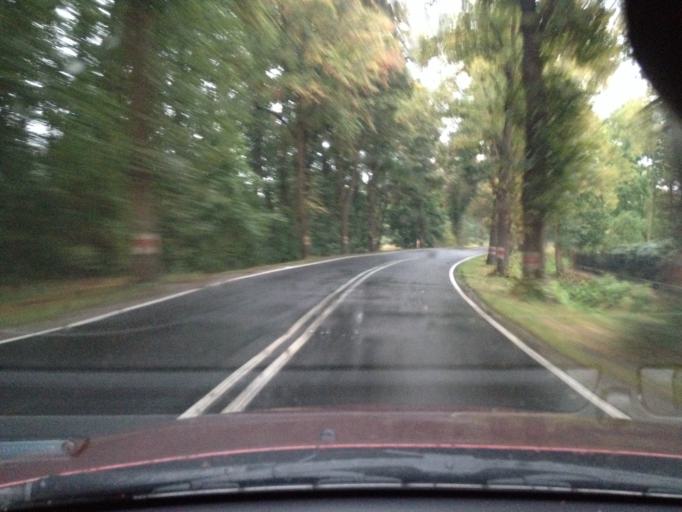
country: PL
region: Lubusz
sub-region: Powiat zaganski
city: Gozdnica
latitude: 51.3971
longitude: 15.1824
